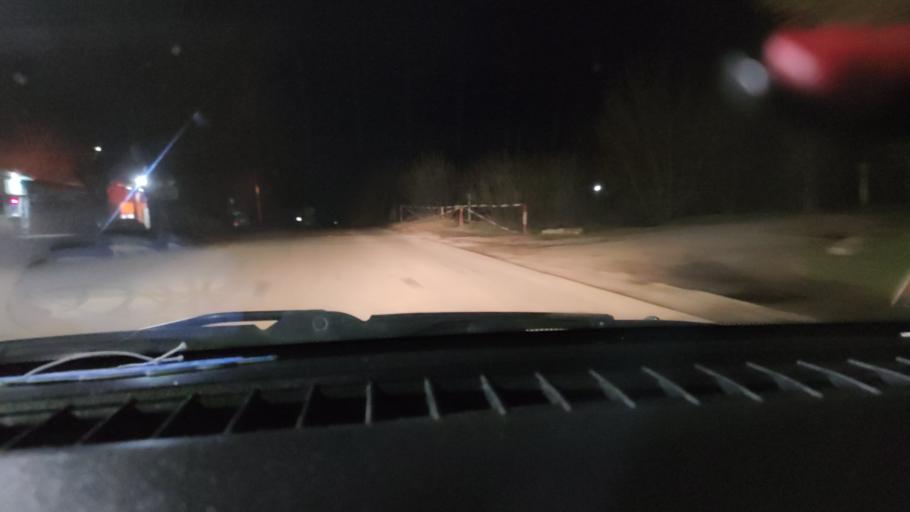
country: RU
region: Saratov
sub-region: Saratovskiy Rayon
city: Saratov
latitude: 51.6150
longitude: 45.9588
